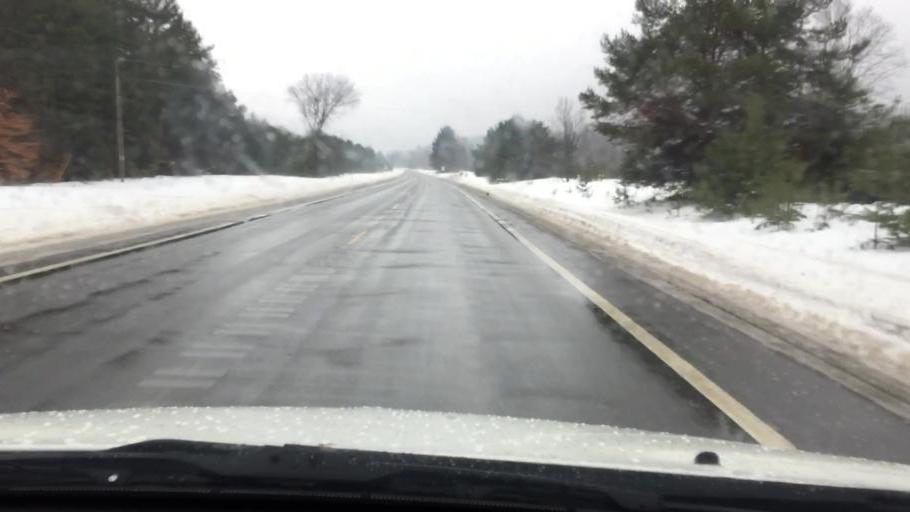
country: US
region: Michigan
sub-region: Charlevoix County
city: East Jordan
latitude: 45.0756
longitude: -85.0875
